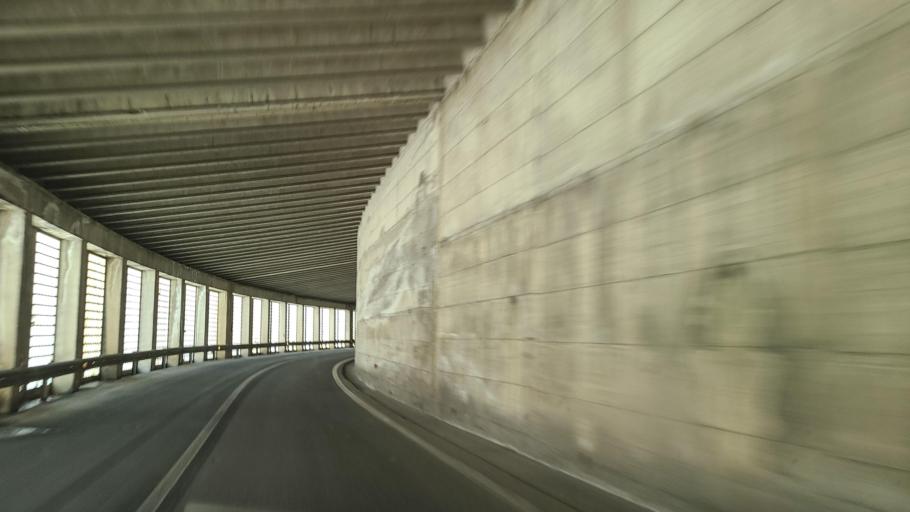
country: IT
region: Lombardy
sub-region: Provincia di Sondrio
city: Livigno
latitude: 46.5873
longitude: 10.1693
